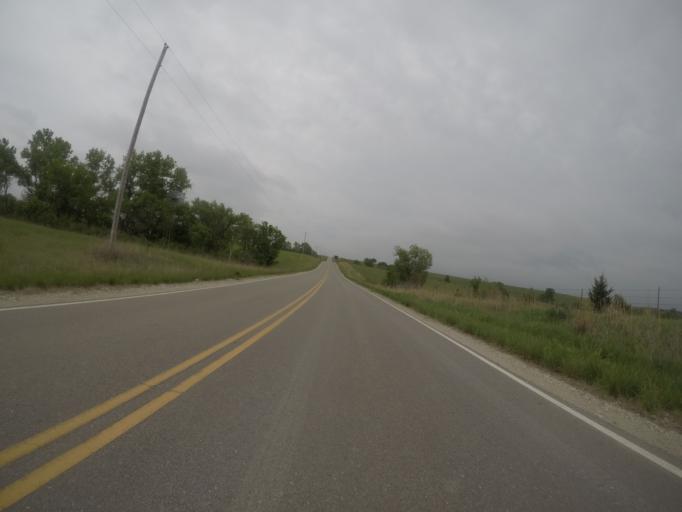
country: US
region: Kansas
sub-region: Pottawatomie County
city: Westmoreland
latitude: 39.5115
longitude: -96.2388
